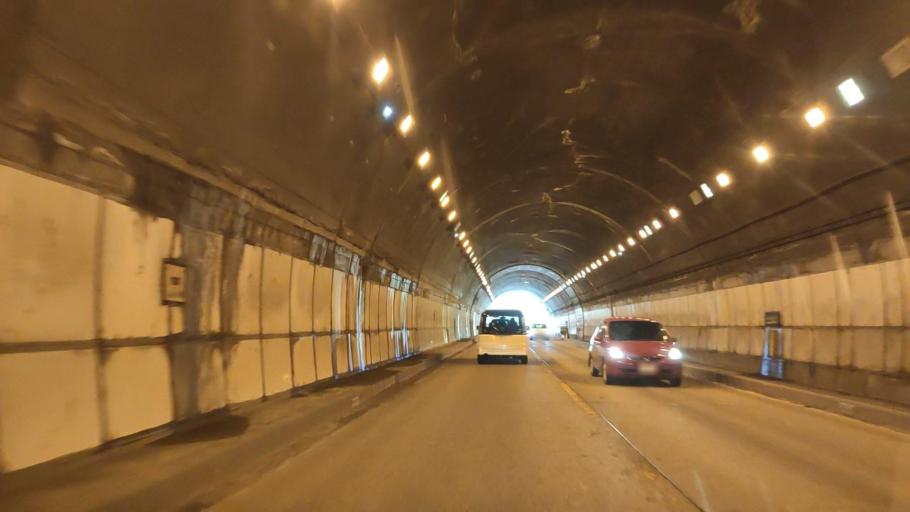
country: JP
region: Aomori
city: Aomori Shi
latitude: 40.8597
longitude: 140.8430
